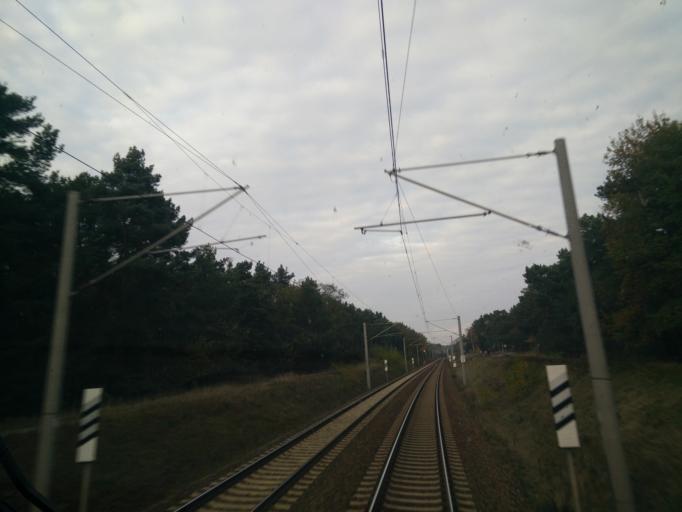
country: DE
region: Brandenburg
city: Bestensee
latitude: 52.2168
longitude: 13.6187
